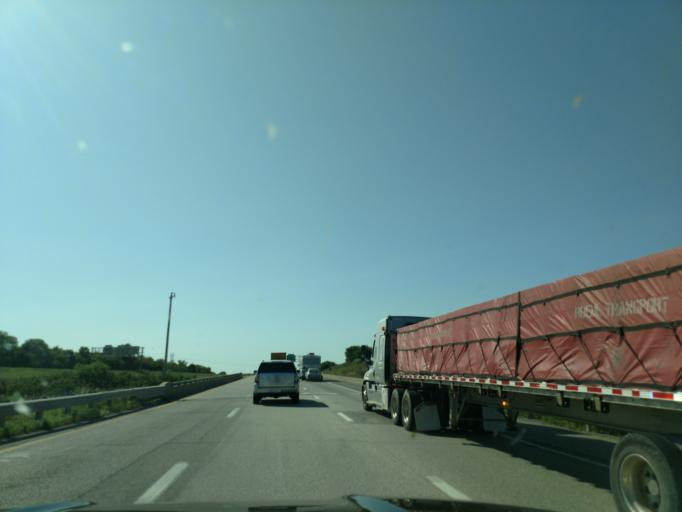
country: US
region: Missouri
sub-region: Andrew County
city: Savannah
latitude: 39.8870
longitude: -94.8574
